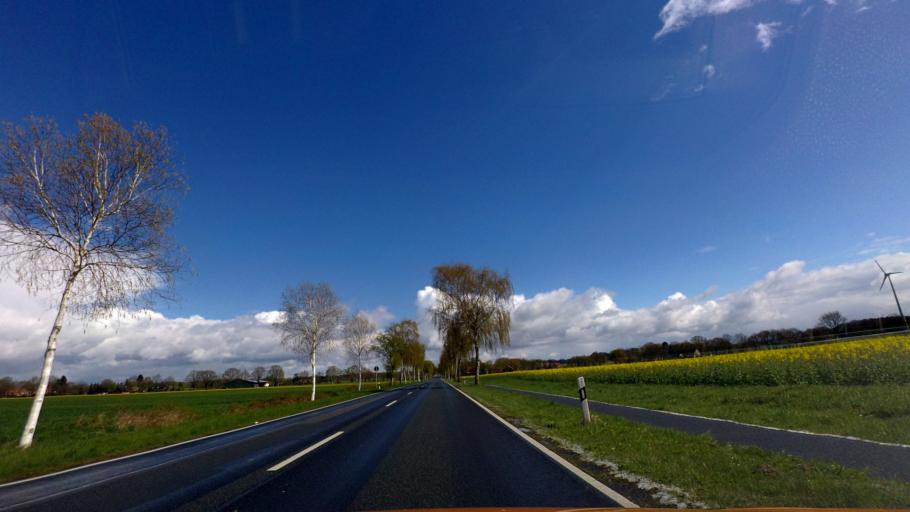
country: DE
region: Lower Saxony
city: Ottersberg
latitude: 53.0687
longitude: 9.0928
